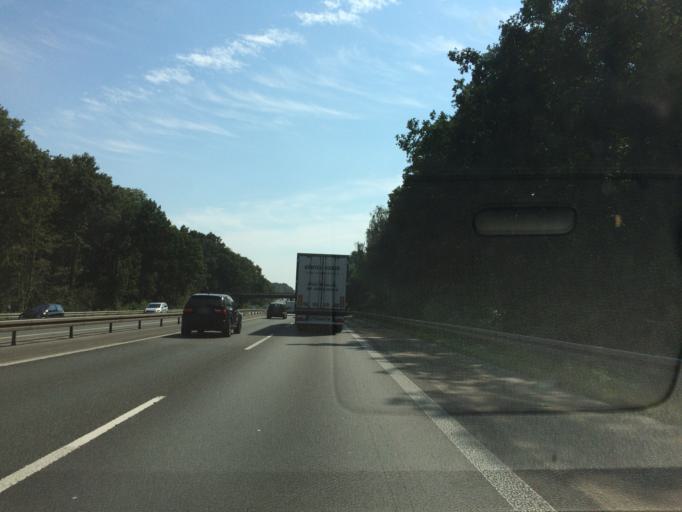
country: DE
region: North Rhine-Westphalia
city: Kamen
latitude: 51.6287
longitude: 7.6865
